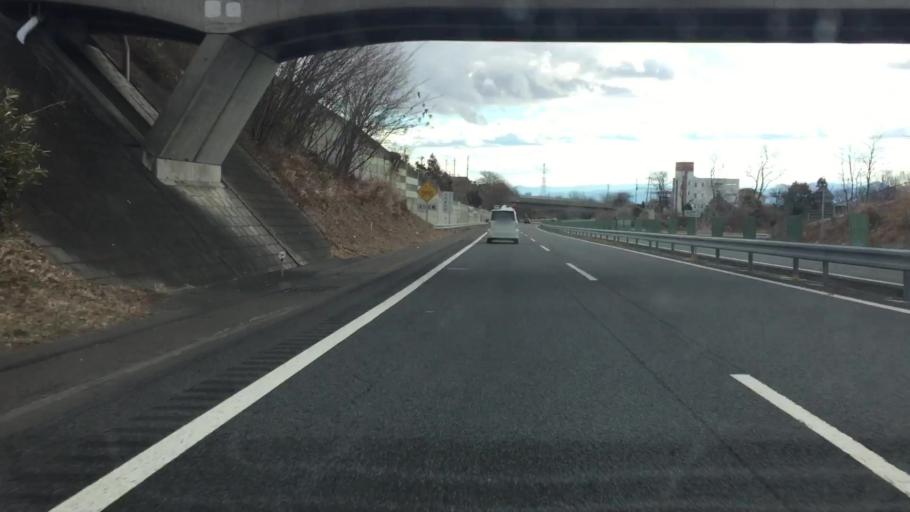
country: JP
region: Gunma
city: Shibukawa
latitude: 36.5076
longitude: 139.0319
